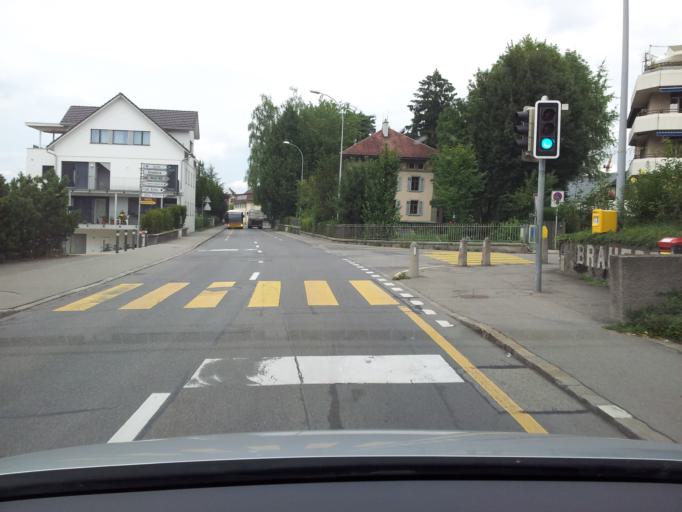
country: CH
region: Lucerne
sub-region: Sursee District
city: Sursee
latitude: 47.1695
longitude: 8.1134
